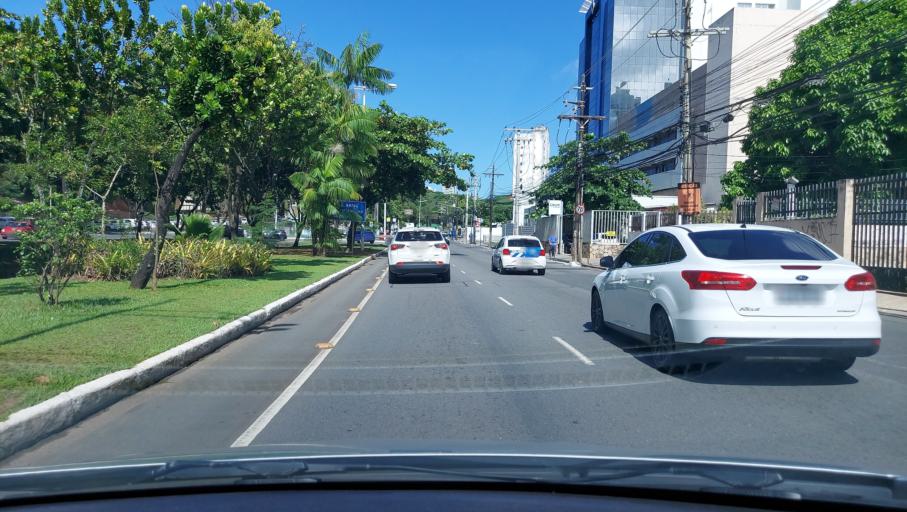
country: BR
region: Bahia
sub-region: Salvador
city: Salvador
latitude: -13.0067
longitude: -38.4995
